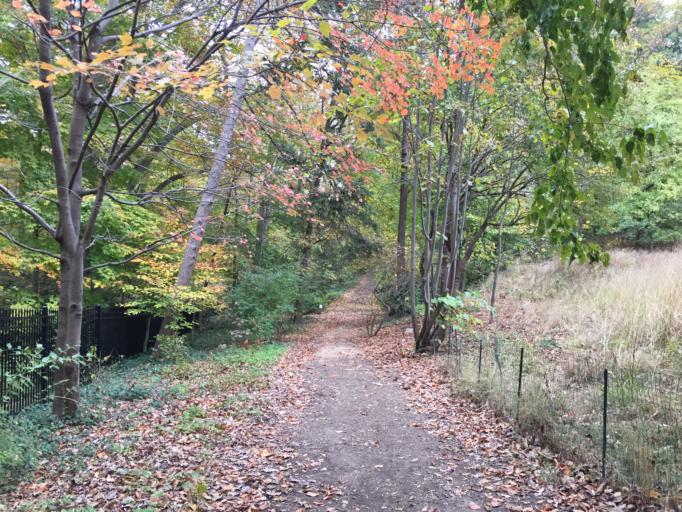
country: US
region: Maryland
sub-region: Montgomery County
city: Chevy Chase Village
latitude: 38.9329
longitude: -77.0603
